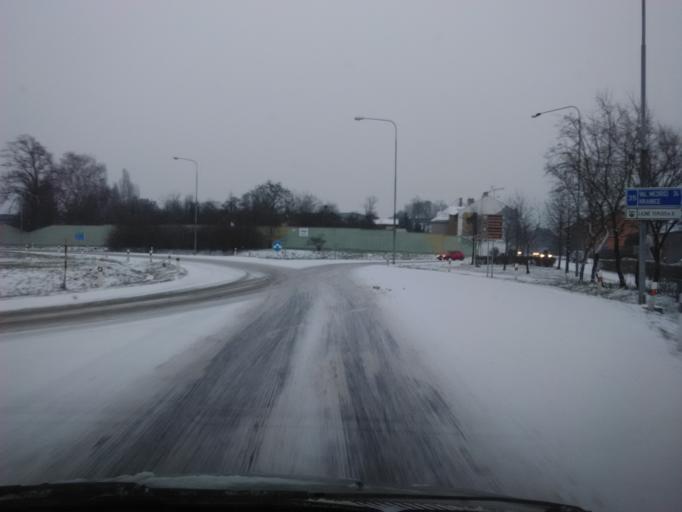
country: CZ
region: Olomoucky
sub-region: Okres Prerov
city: Hranice
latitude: 49.5523
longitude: 17.7151
